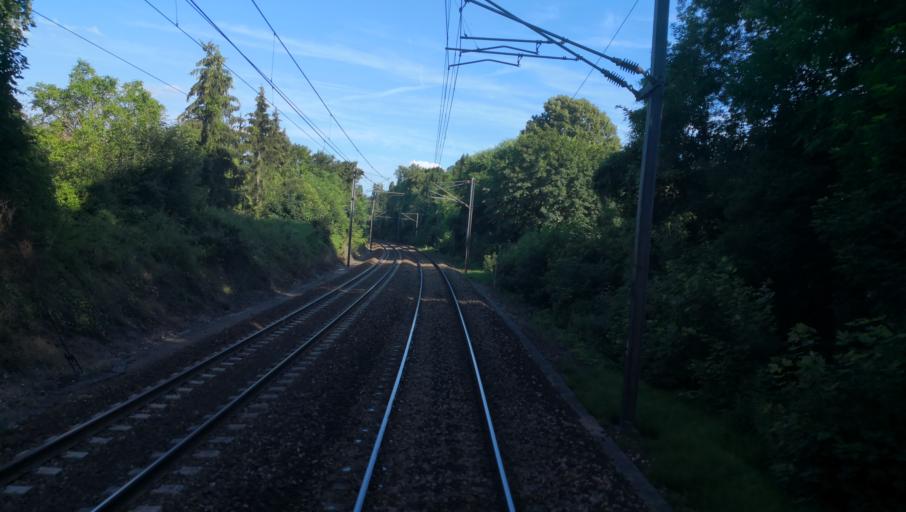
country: FR
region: Ile-de-France
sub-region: Departement des Yvelines
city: Villennes-sur-Seine
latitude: 48.9332
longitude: 2.0032
